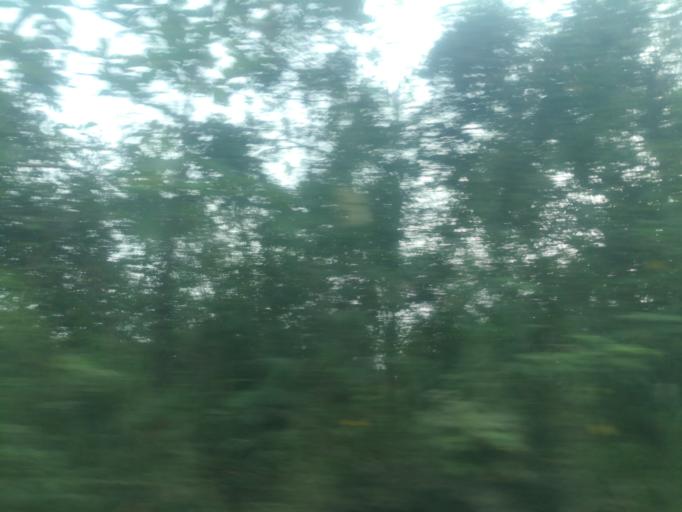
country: NG
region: Ogun
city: Abeokuta
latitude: 7.1973
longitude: 3.2265
